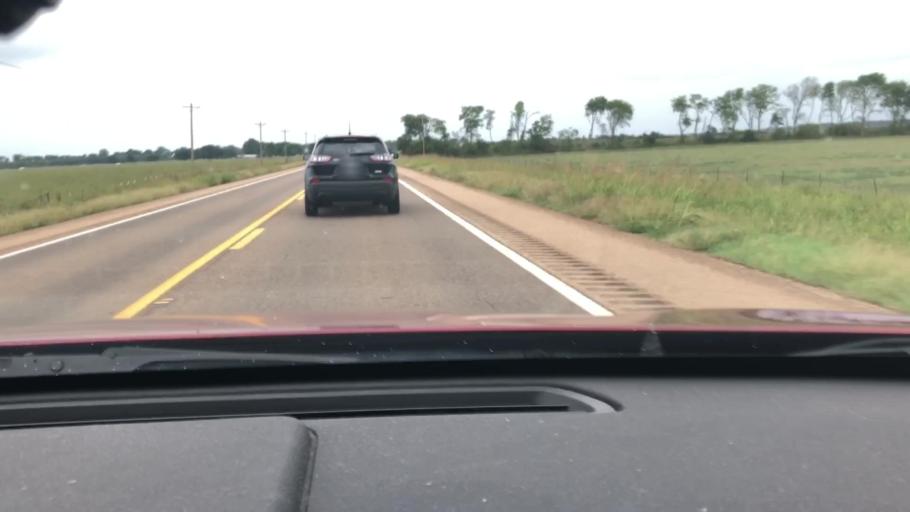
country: US
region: Arkansas
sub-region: Lafayette County
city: Lewisville
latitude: 33.3838
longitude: -93.7361
